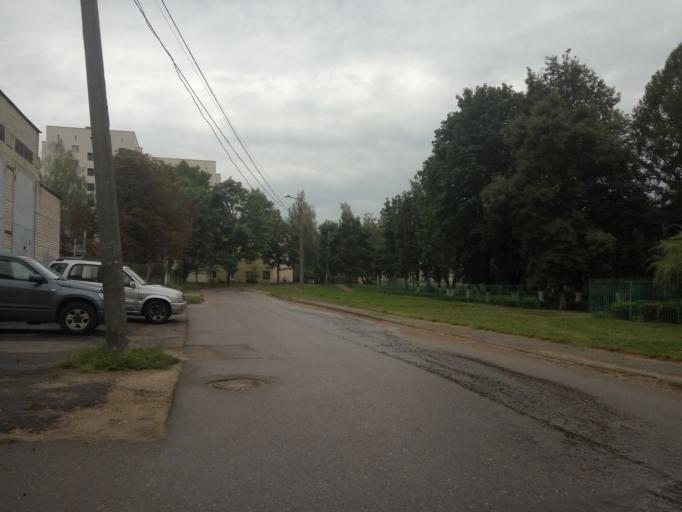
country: BY
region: Vitebsk
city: Vitebsk
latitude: 55.1973
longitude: 30.2476
